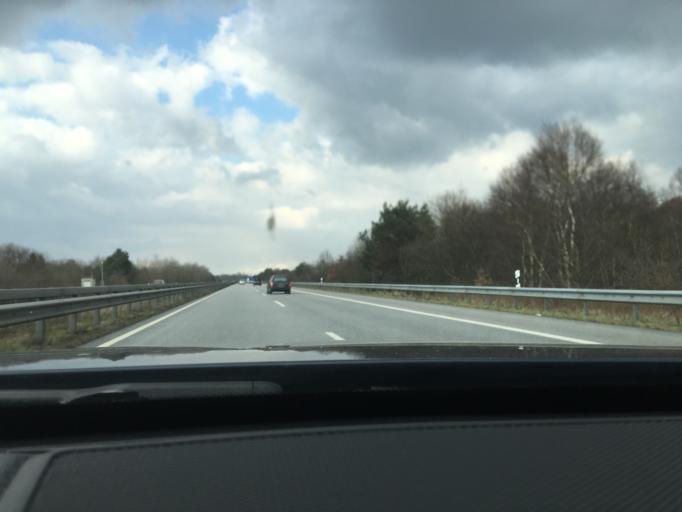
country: DE
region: Lower Saxony
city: Uthlede
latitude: 53.3533
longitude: 8.5929
